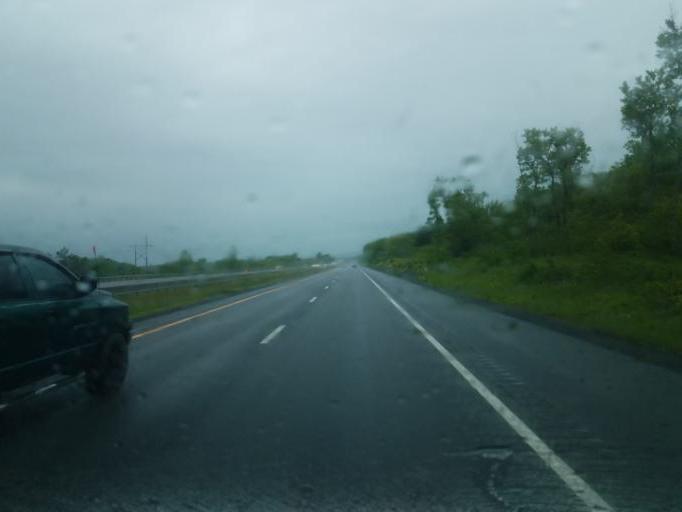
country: US
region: New York
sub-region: Herkimer County
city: Frankfort
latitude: 43.0387
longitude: -75.0509
